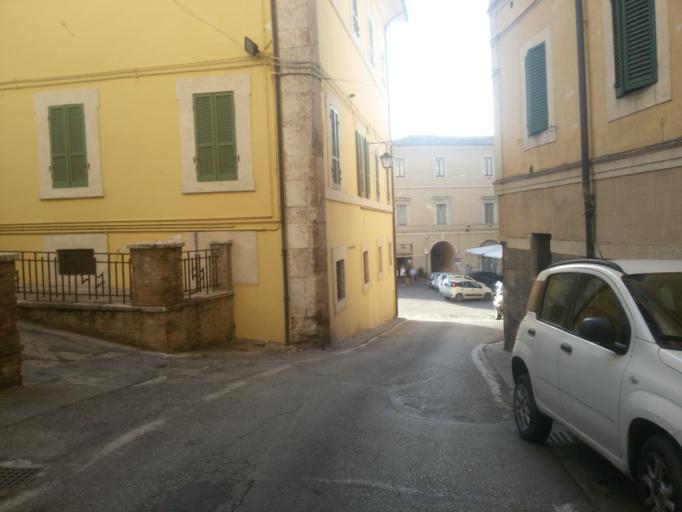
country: IT
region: Umbria
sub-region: Provincia di Perugia
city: Spoleto
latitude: 42.7332
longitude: 12.7362
